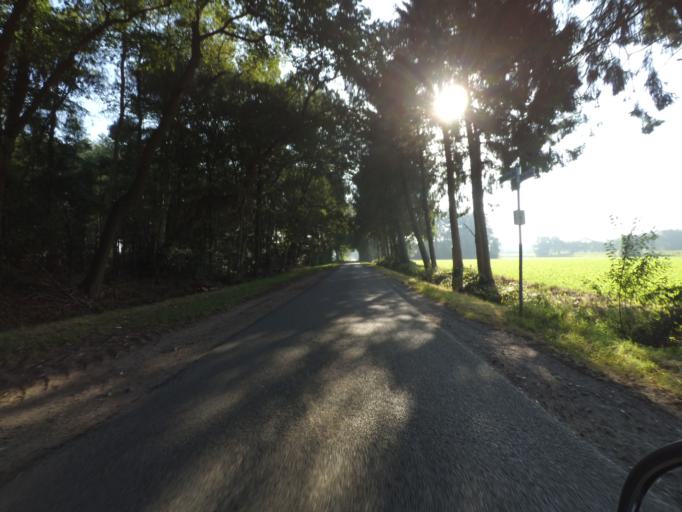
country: DE
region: Lower Saxony
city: Ohne
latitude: 52.2744
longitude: 7.2572
